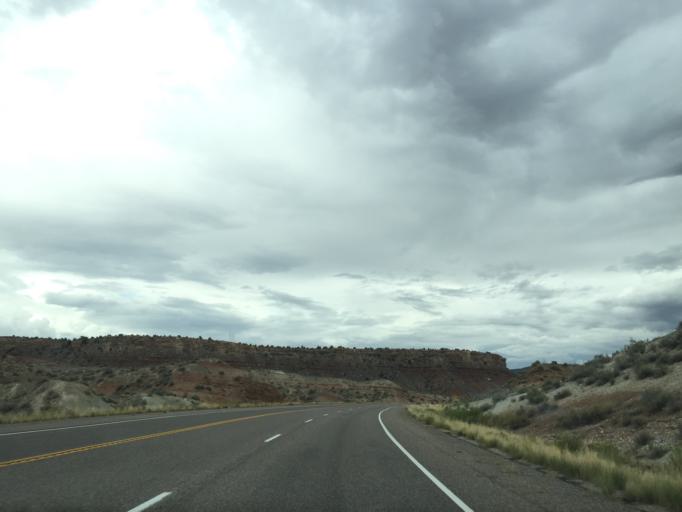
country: US
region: Utah
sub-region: Washington County
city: Hildale
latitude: 37.1707
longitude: -113.0693
